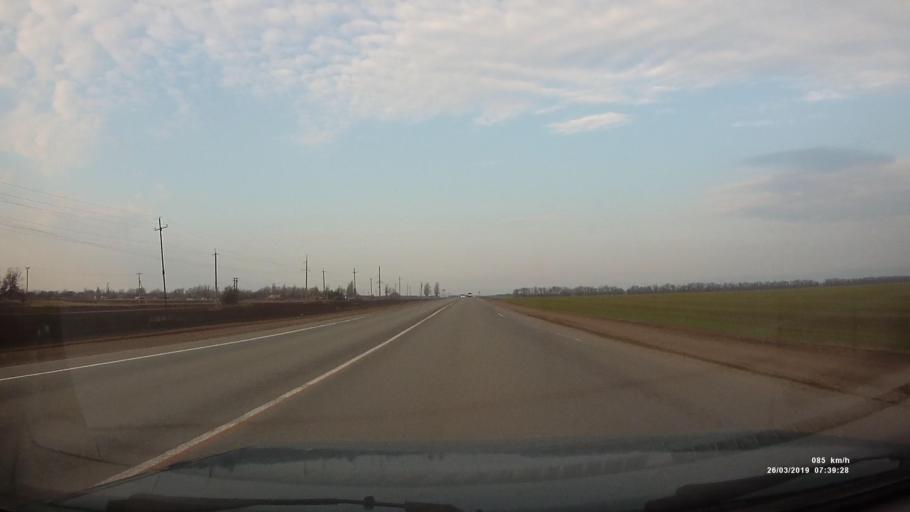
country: RU
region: Rostov
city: Novobessergenovka
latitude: 47.1972
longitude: 38.6634
